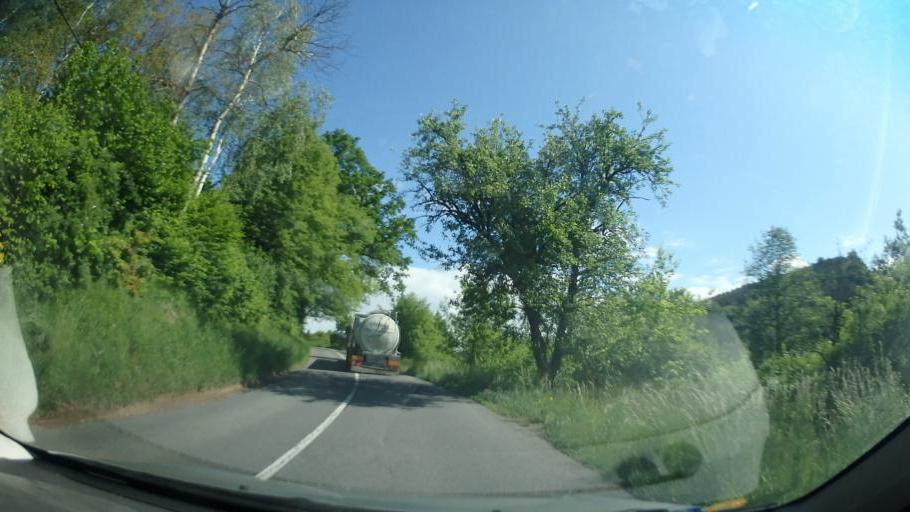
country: CZ
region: Pardubicky
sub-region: Okres Svitavy
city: Moravska Trebova
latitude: 49.7136
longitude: 16.6373
